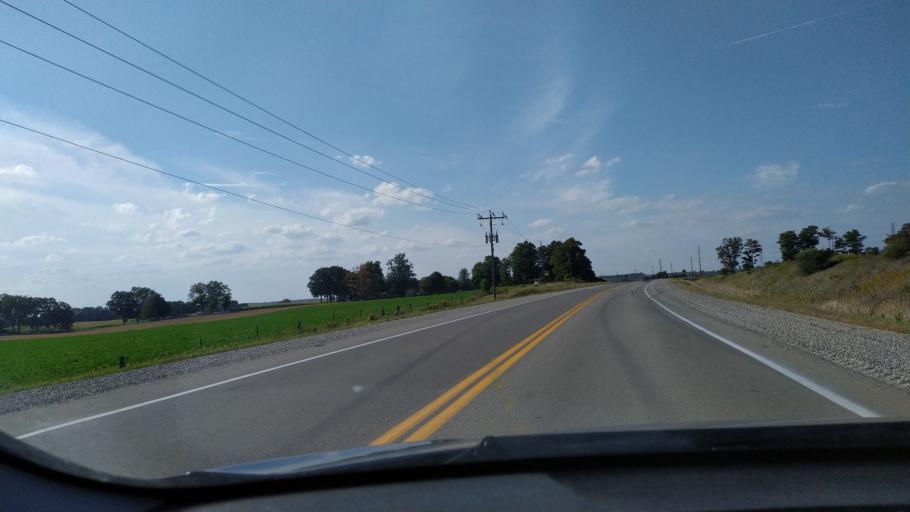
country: CA
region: Ontario
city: Ingersoll
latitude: 43.0614
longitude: -80.8359
